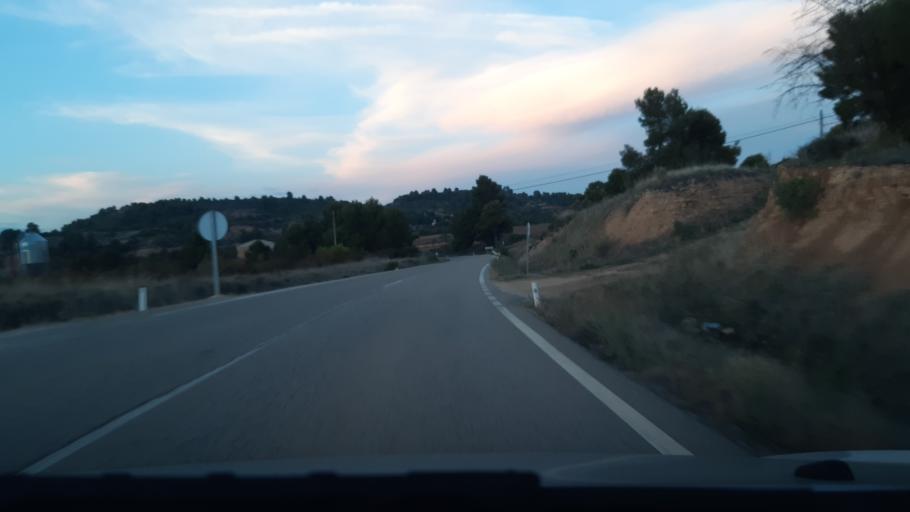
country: ES
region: Aragon
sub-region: Provincia de Teruel
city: Valderrobres
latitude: 40.8608
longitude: 0.1692
